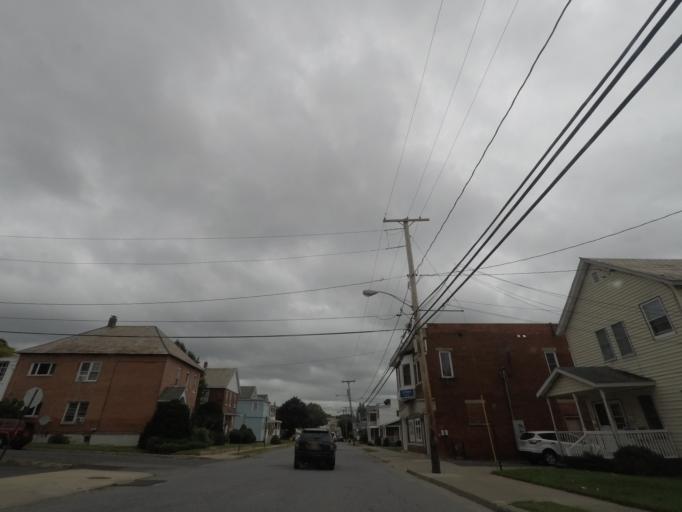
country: US
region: New York
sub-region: Saratoga County
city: Mechanicville
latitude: 42.9108
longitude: -73.6934
